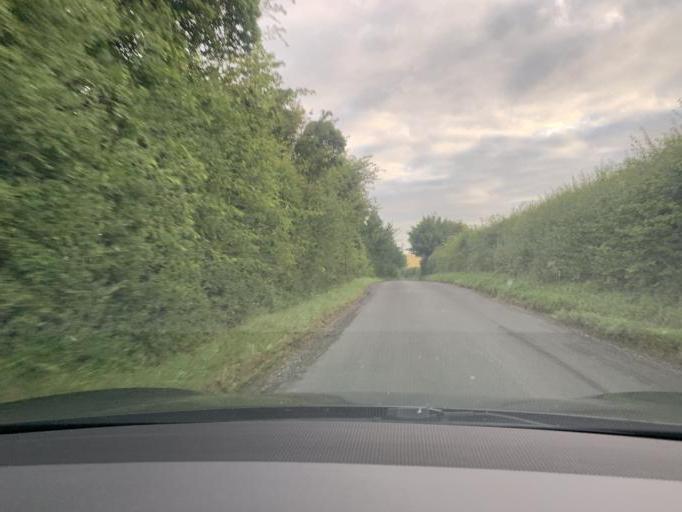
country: GB
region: England
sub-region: Wiltshire
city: Collingbourne Kingston
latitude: 51.2717
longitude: -1.6419
